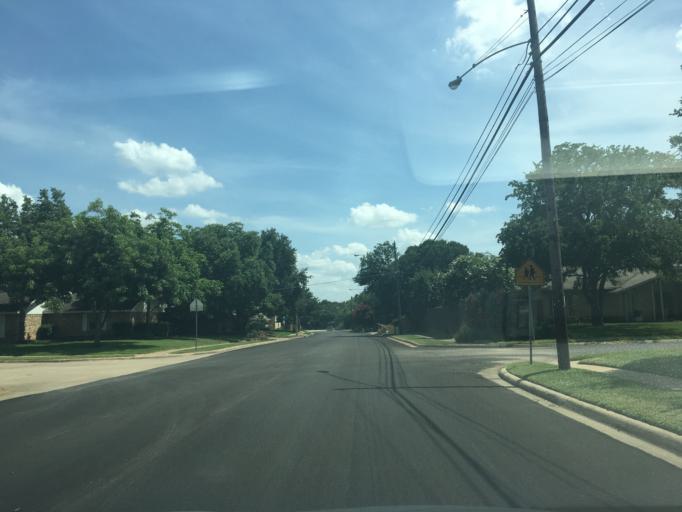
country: US
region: Texas
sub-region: Dallas County
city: Addison
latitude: 32.9174
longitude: -96.8467
